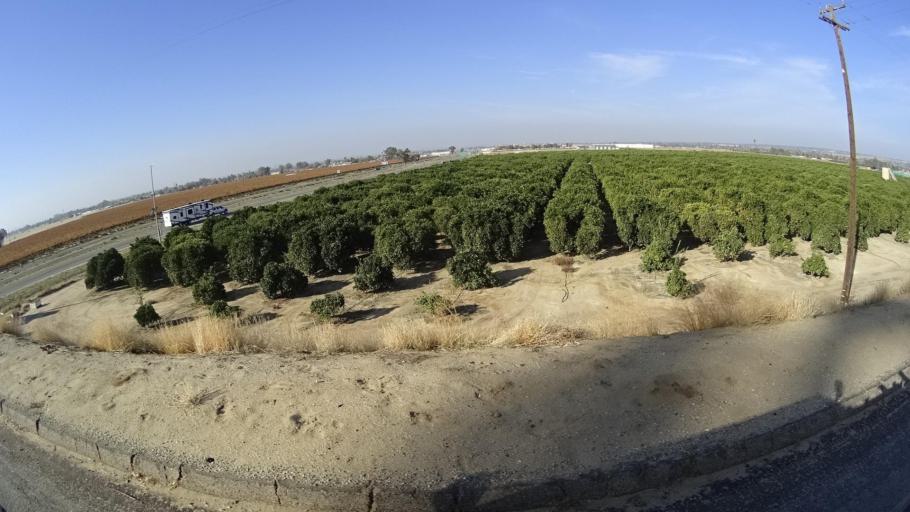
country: US
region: California
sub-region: Kern County
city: Lamont
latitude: 35.3515
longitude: -118.8963
